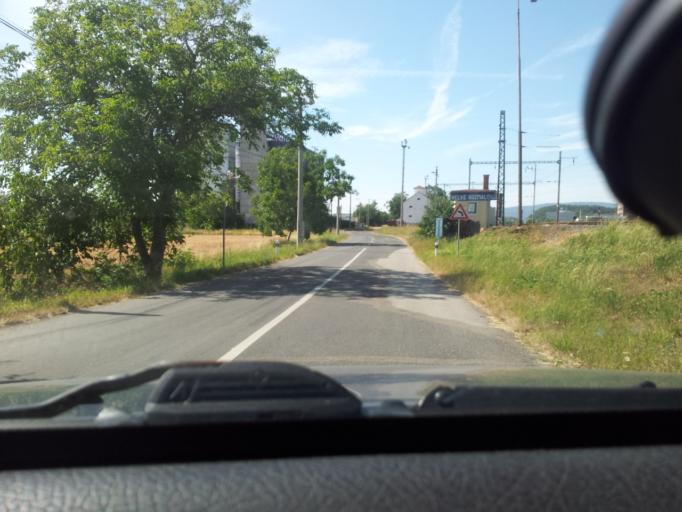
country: SK
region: Nitriansky
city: Tlmace
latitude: 48.2783
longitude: 18.5514
